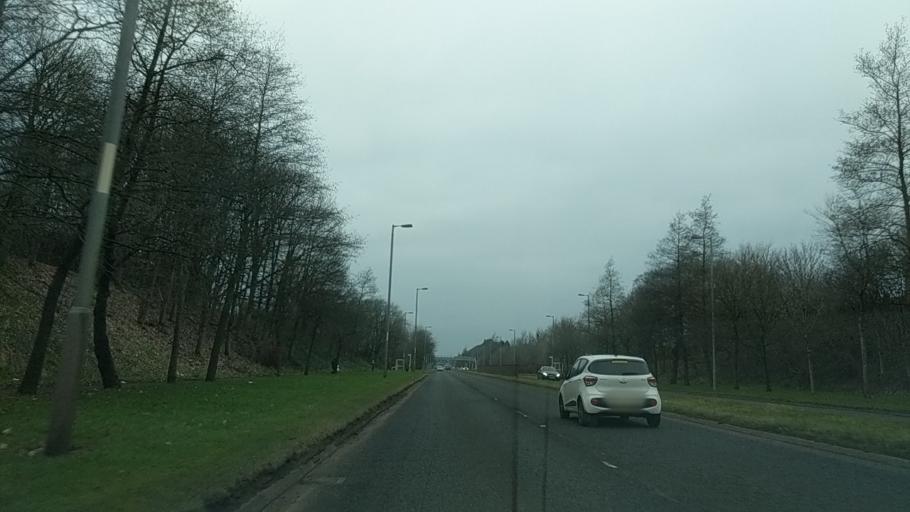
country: GB
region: Scotland
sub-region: South Lanarkshire
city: East Kilbride
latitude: 55.7615
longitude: -4.1931
